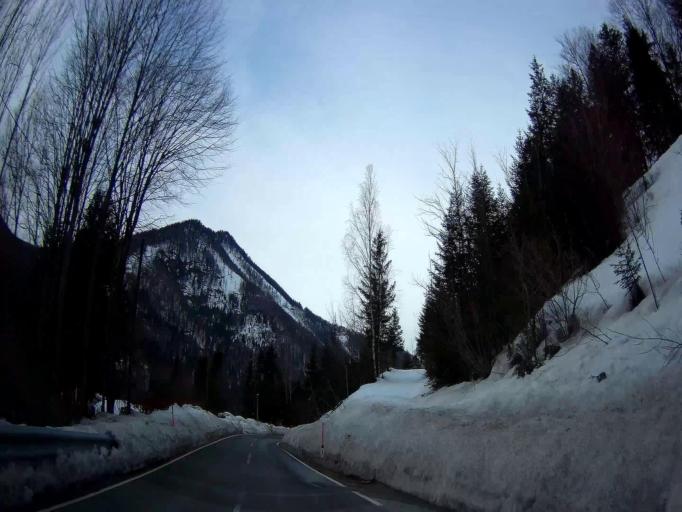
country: AT
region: Salzburg
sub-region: Politischer Bezirk Hallein
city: Krispl
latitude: 47.7424
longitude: 13.1707
